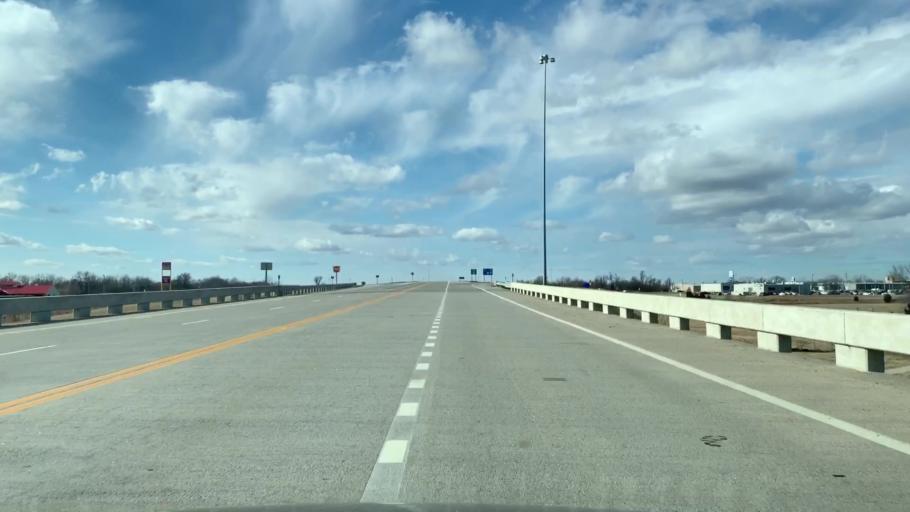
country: US
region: Kansas
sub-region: Labette County
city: Parsons
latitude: 37.3659
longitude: -95.2531
